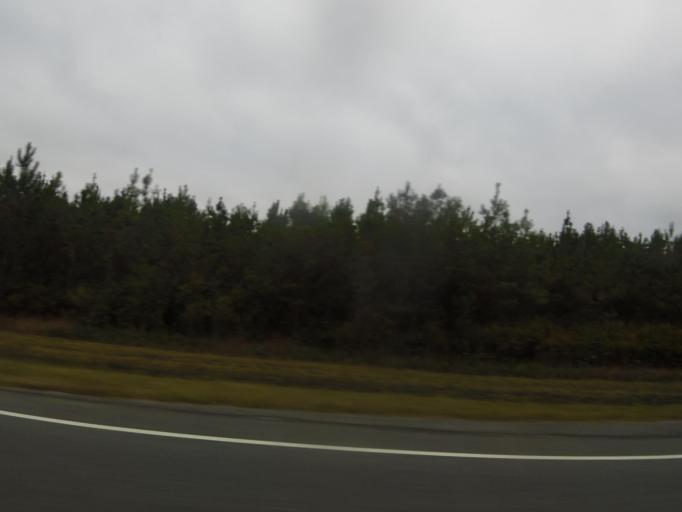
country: US
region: Georgia
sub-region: Charlton County
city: Folkston
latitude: 30.9120
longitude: -82.0773
